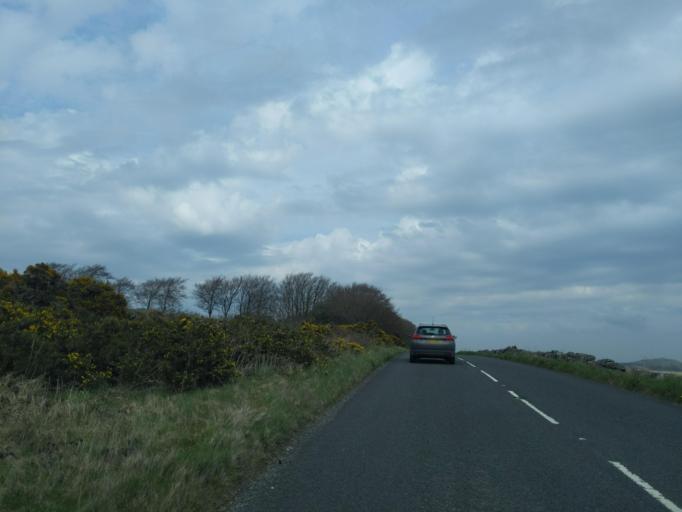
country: GB
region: England
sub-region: Devon
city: Yelverton
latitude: 50.5650
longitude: -3.9502
